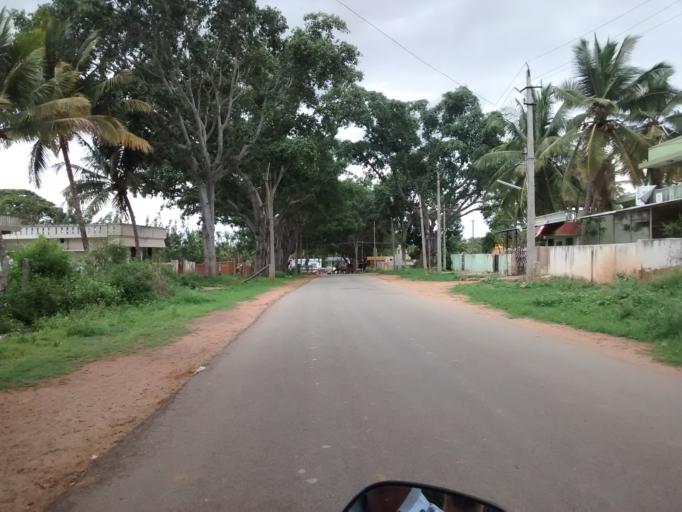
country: IN
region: Karnataka
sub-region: Tumkur
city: Kunigal
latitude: 13.1372
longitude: 77.1497
